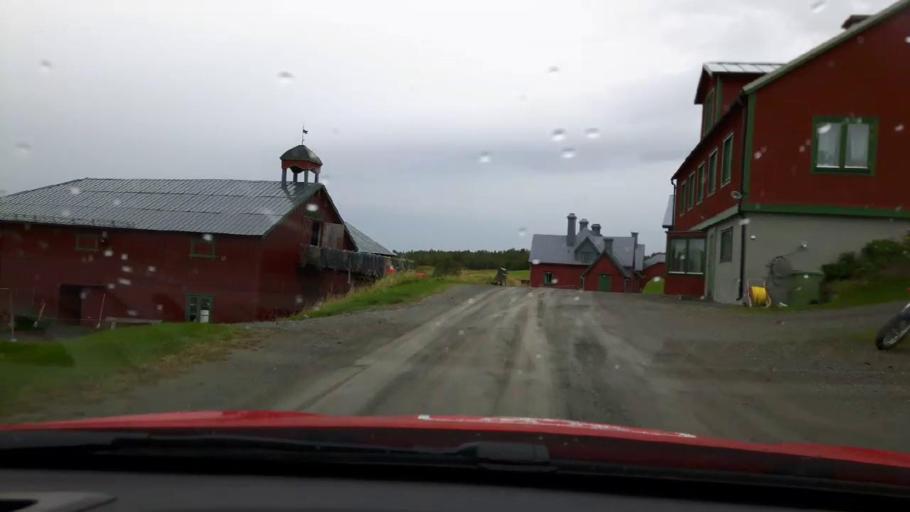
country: NO
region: Nord-Trondelag
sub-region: Meraker
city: Meraker
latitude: 63.5739
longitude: 12.2762
